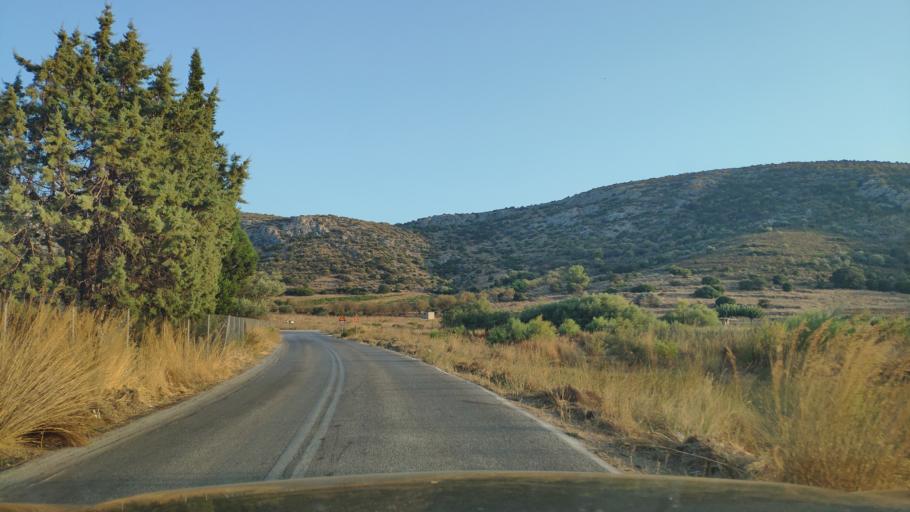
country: GR
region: Attica
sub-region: Nomarchia Anatolikis Attikis
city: Limin Mesoyaias
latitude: 37.9230
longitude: 23.9940
